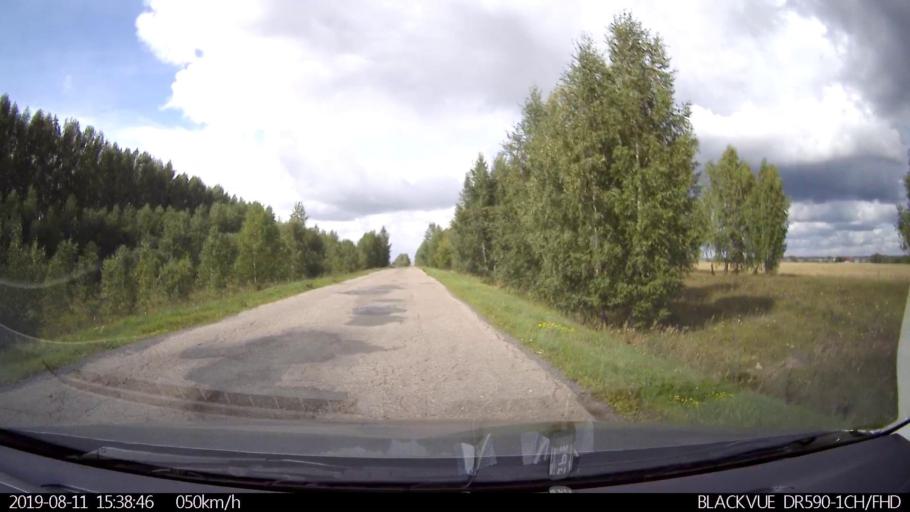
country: RU
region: Ulyanovsk
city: Ignatovka
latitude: 53.8636
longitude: 47.6401
